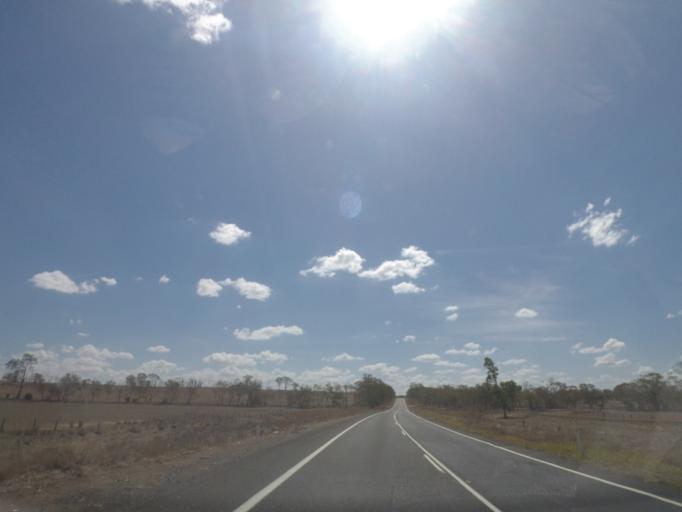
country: AU
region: Queensland
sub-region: Southern Downs
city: Warwick
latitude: -28.2059
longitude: 151.5811
